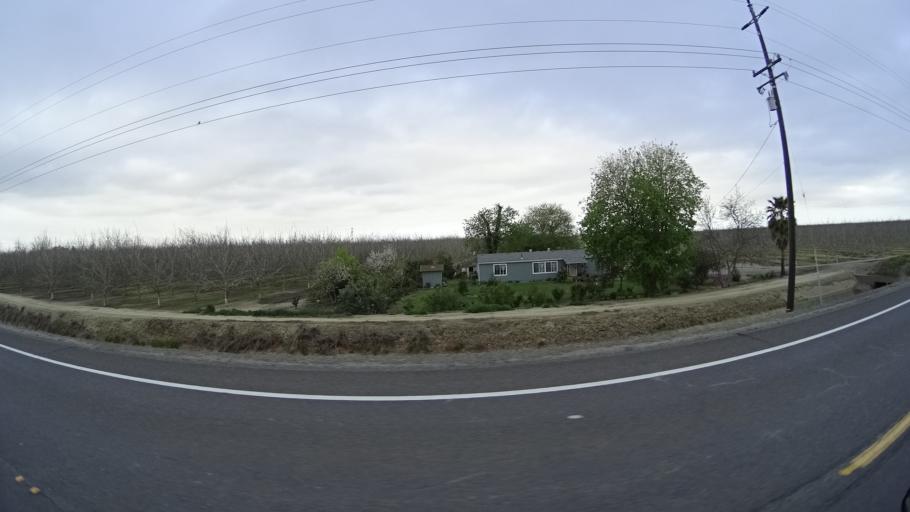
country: US
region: California
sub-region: Colusa County
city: Colusa
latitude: 39.4170
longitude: -122.0106
